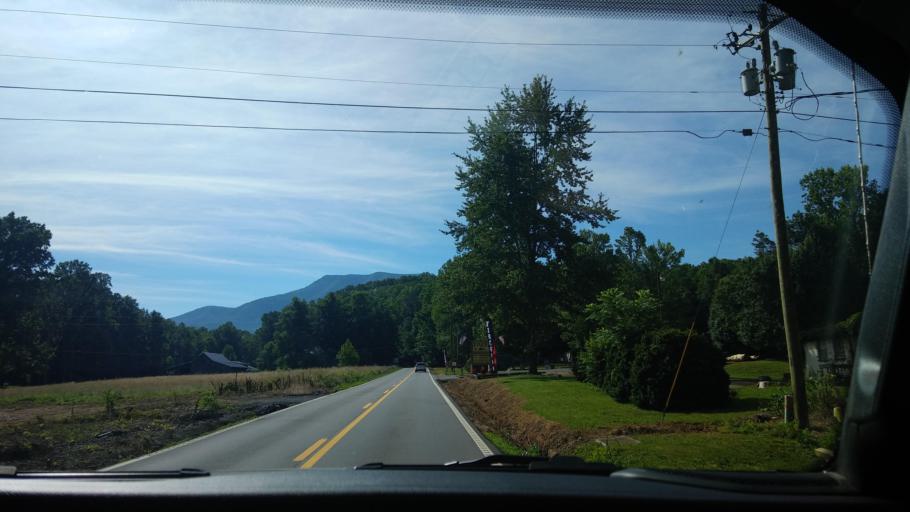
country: US
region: Tennessee
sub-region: Cocke County
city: Newport
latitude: 35.7846
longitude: -83.2232
